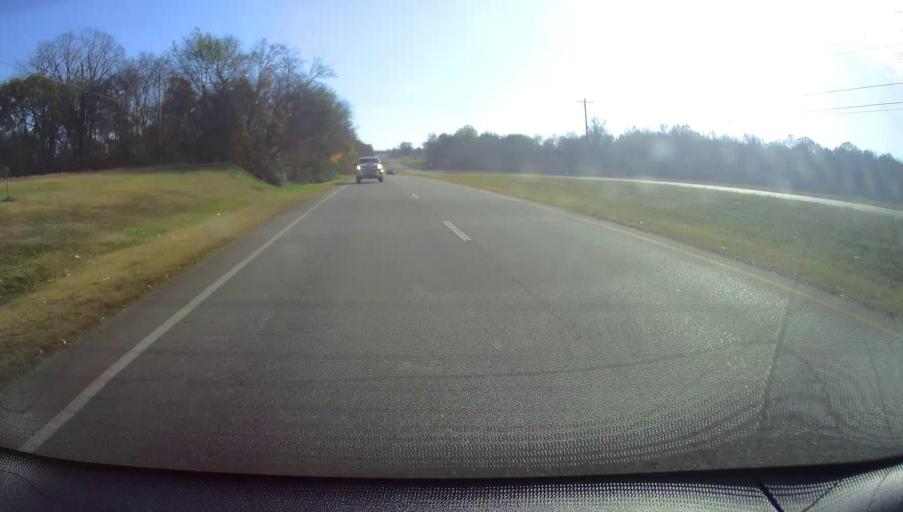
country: US
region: Alabama
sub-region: Limestone County
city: Athens
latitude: 34.7418
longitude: -86.9570
